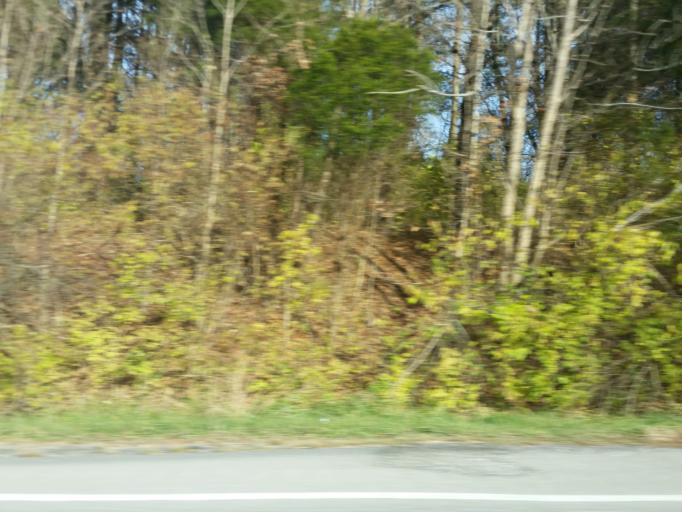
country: US
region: Kentucky
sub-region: Campbell County
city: Claryville
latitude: 38.8437
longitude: -84.3751
